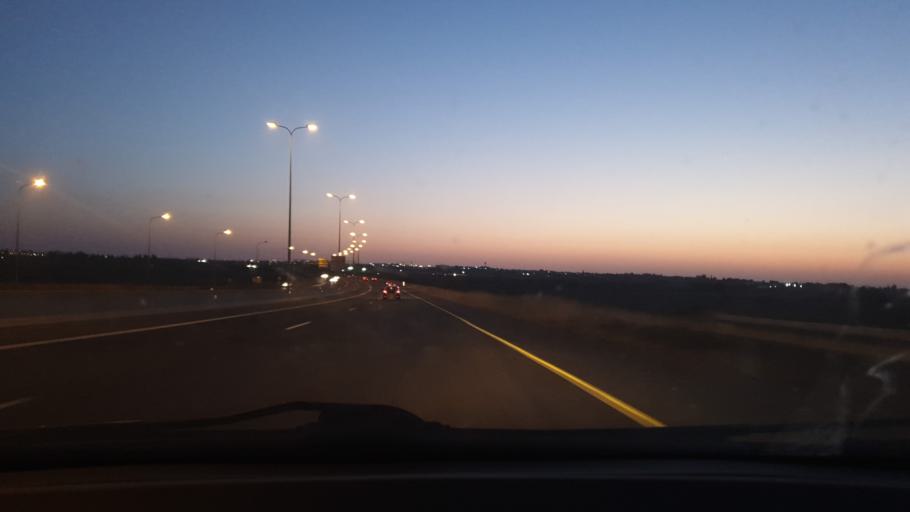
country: IL
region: Central District
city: Gedera
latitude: 31.8055
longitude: 34.8259
